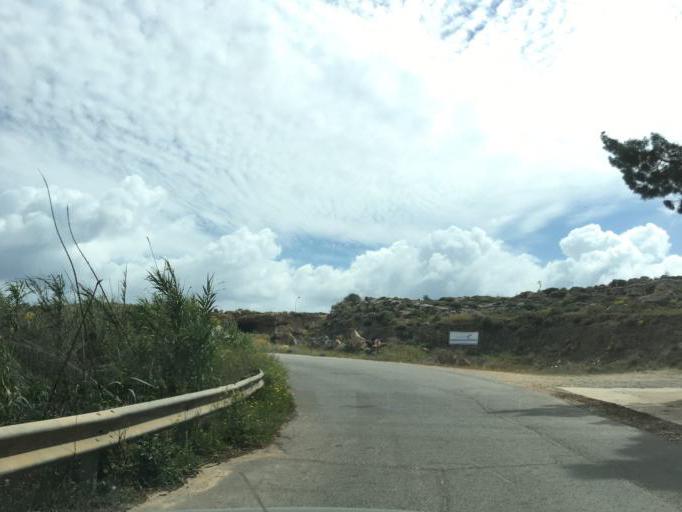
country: CY
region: Ammochostos
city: Liopetri
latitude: 34.9750
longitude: 33.8943
